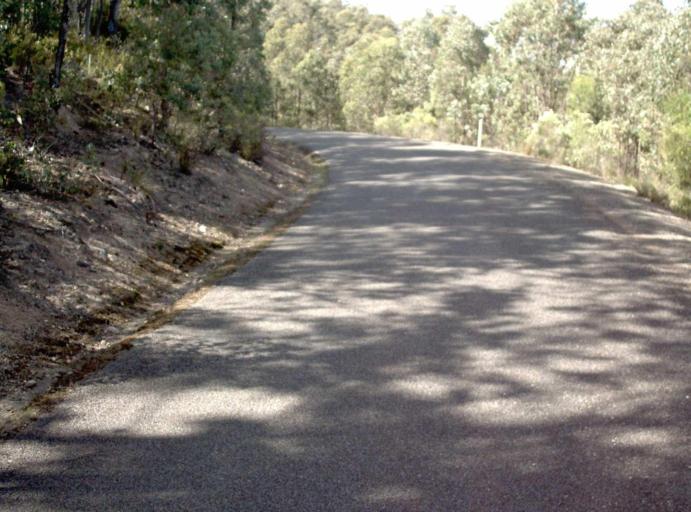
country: AU
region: Victoria
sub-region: East Gippsland
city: Lakes Entrance
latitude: -37.4766
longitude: 148.1244
